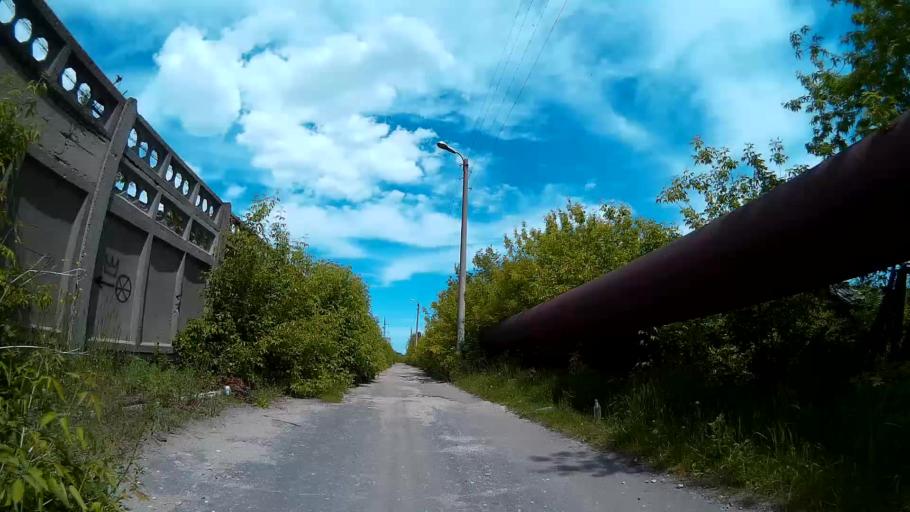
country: RU
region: Ulyanovsk
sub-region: Ulyanovskiy Rayon
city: Ulyanovsk
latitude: 54.2824
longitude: 48.3629
